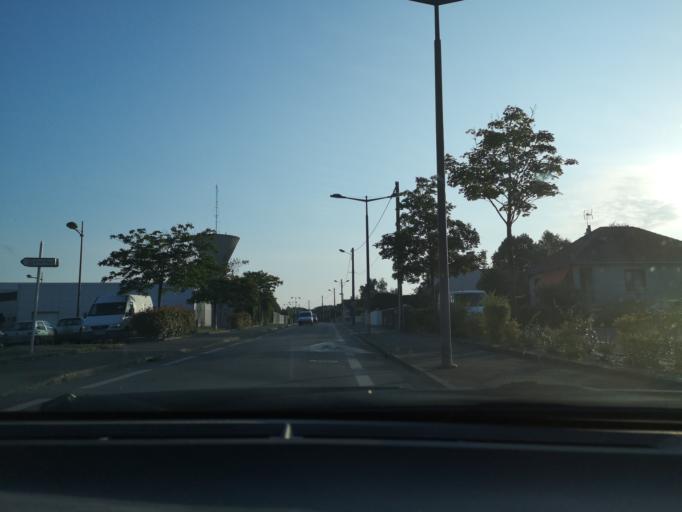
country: FR
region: Centre
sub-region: Departement du Loiret
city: Fleury-les-Aubrais
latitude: 47.9286
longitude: 1.9259
